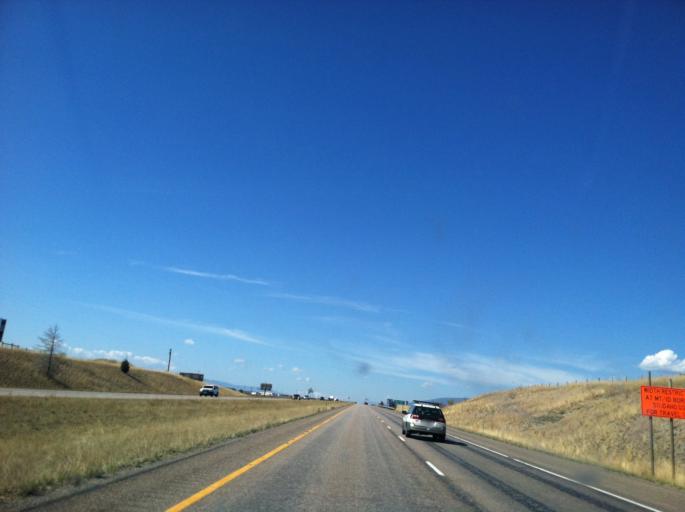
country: US
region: Montana
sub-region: Missoula County
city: Orchard Homes
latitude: 46.9421
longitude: -114.1149
